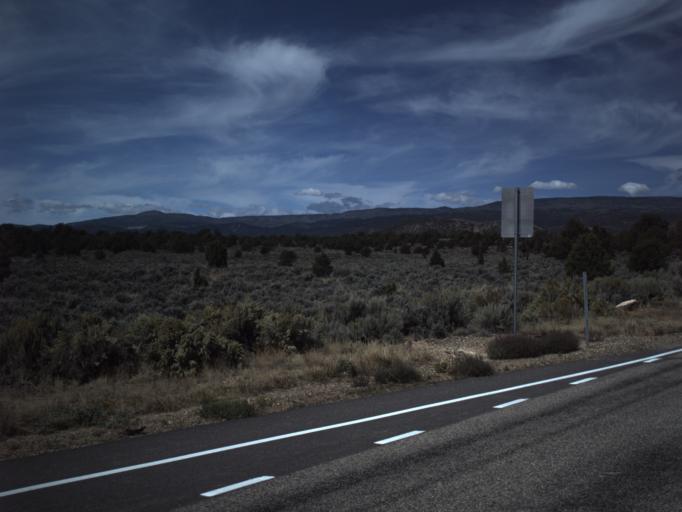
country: US
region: Utah
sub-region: Wayne County
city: Loa
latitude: 37.8842
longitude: -111.4578
